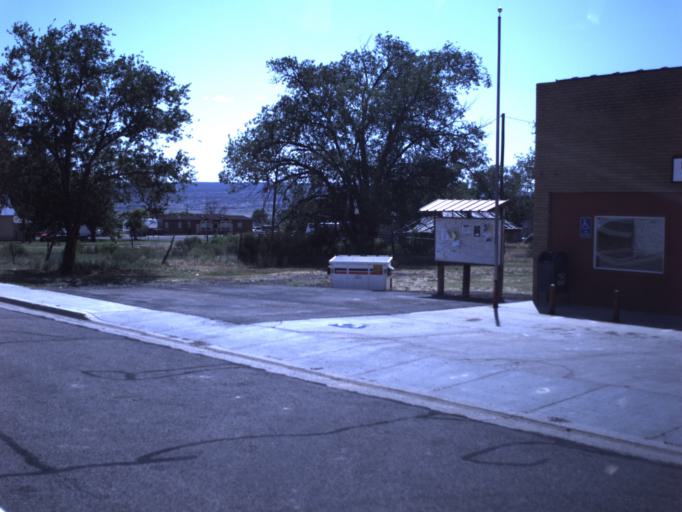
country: US
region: Utah
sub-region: Emery County
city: Ferron
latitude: 38.9231
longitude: -111.2484
